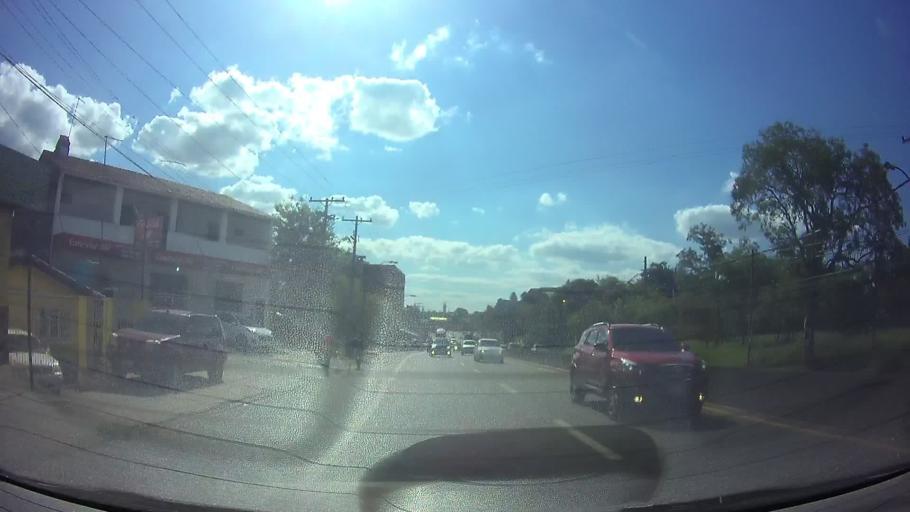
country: PY
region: Central
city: Itaugua
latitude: -25.3966
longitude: -57.3442
